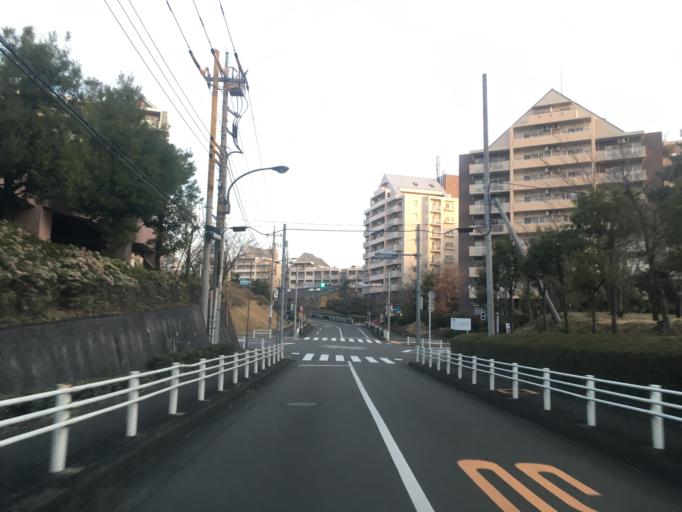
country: JP
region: Tokyo
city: Hachioji
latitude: 35.6150
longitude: 139.3732
